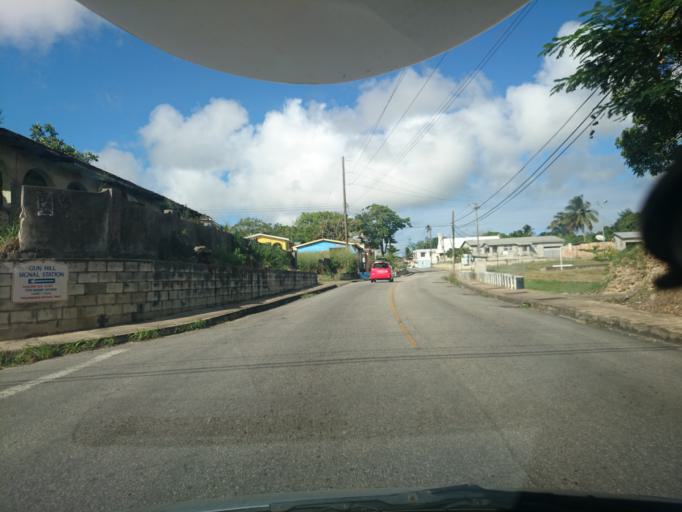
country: BB
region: Saint Thomas
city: Welchman Hall
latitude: 13.1459
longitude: -59.5537
